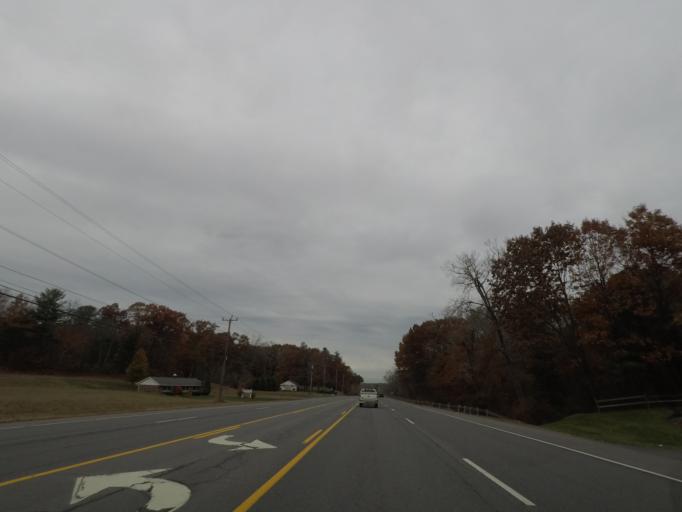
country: US
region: New York
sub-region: Saratoga County
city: Country Knolls
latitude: 42.8833
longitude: -73.7739
